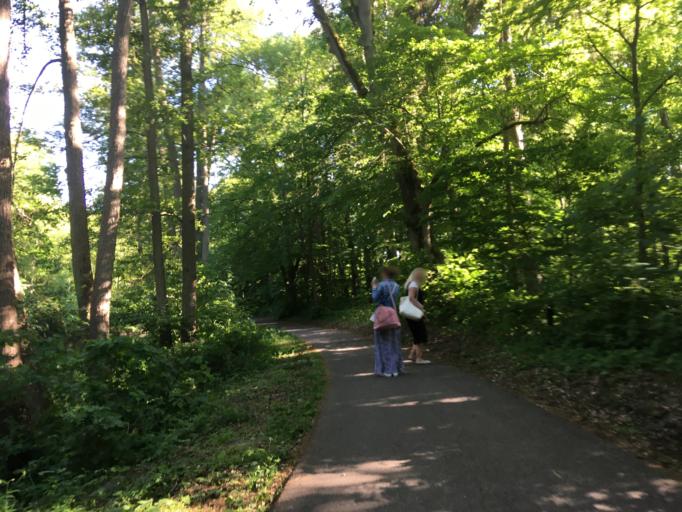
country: DE
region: Brandenburg
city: Marienwerder
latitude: 52.9029
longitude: 13.6493
